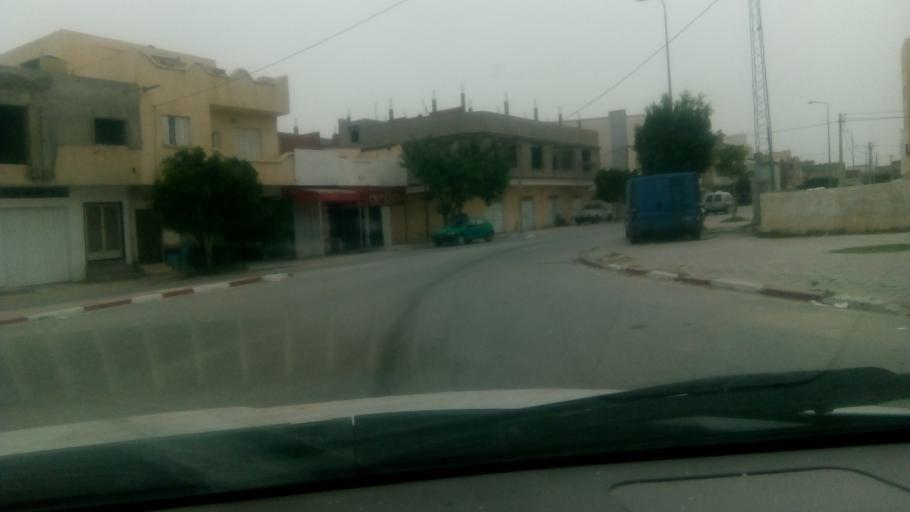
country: TN
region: Al Qayrawan
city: Kairouan
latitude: 35.6715
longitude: 10.0879
